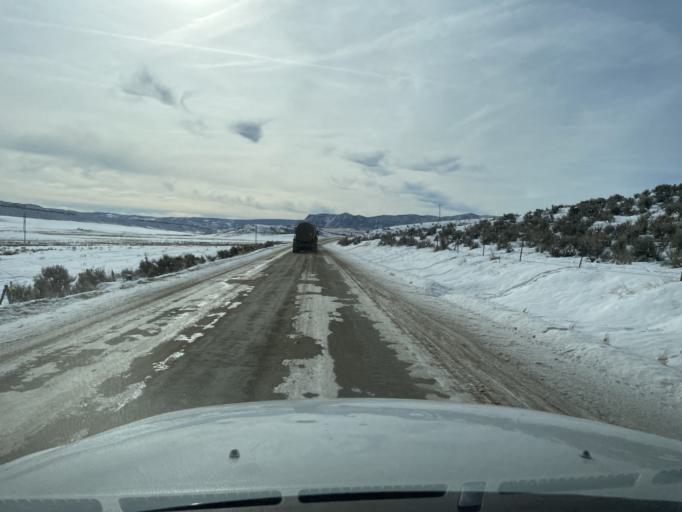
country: US
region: Colorado
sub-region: Moffat County
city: Craig
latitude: 40.3261
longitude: -107.6870
